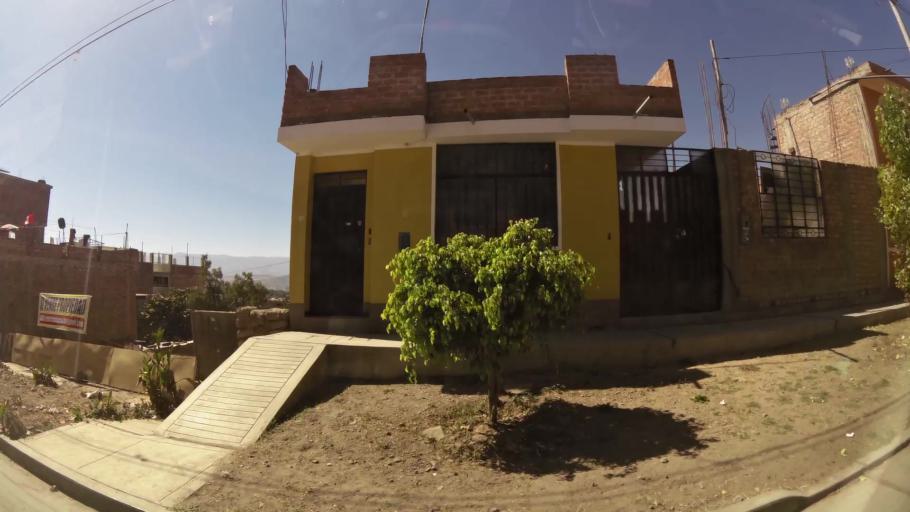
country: PE
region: Ayacucho
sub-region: Provincia de Huamanga
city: Ayacucho
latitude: -13.1494
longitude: -74.2313
